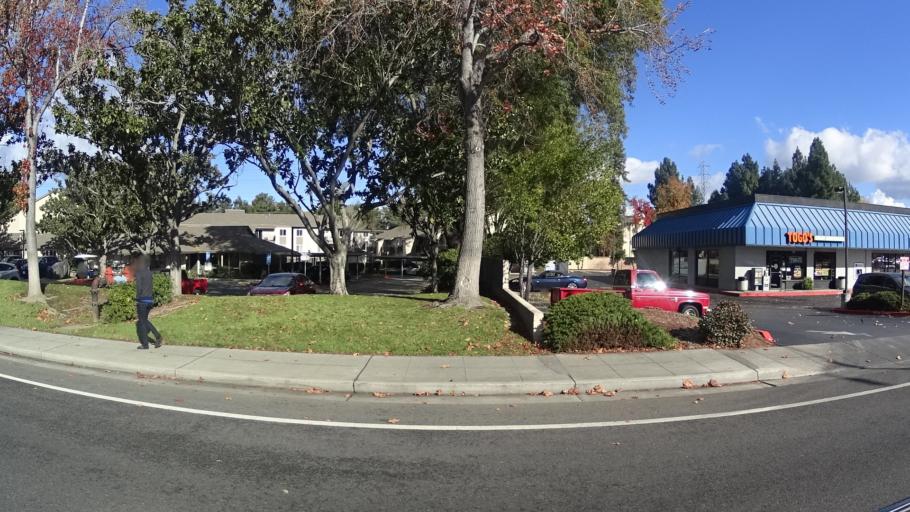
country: US
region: California
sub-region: Santa Clara County
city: Sunnyvale
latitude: 37.3635
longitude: -122.0270
